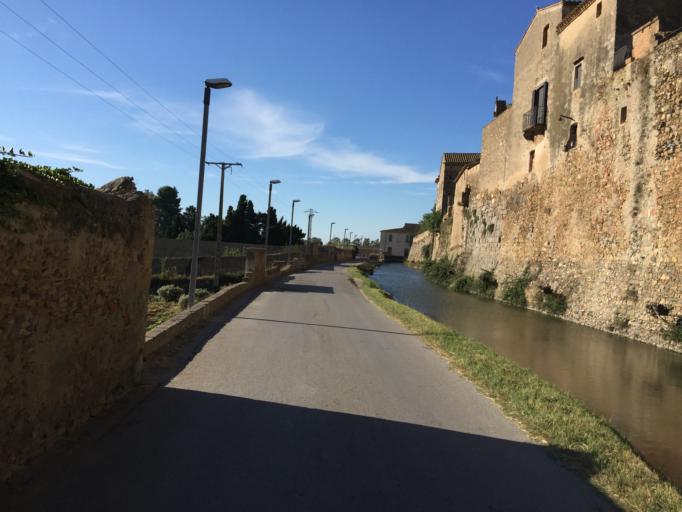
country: ES
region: Catalonia
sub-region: Provincia de Girona
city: Castello d'Empuries
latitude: 42.2605
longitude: 3.0765
